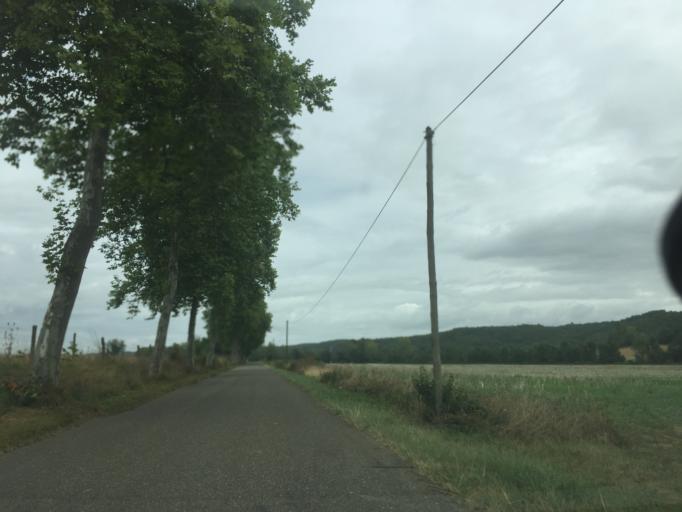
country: FR
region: Midi-Pyrenees
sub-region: Departement du Gers
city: Mielan
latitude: 43.5170
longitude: 0.3247
